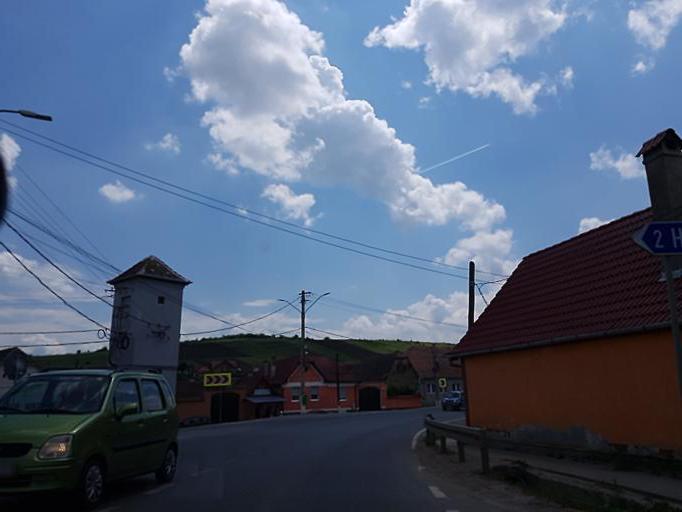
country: RO
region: Sibiu
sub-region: Comuna Sura Mare
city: Sura Mare
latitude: 45.8548
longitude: 24.1704
